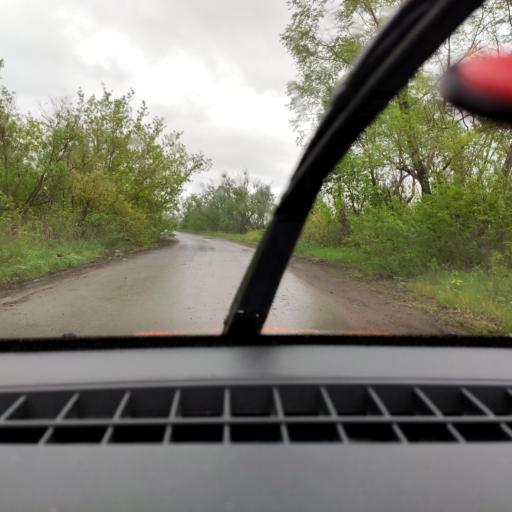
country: RU
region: Bashkortostan
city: Avdon
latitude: 54.5791
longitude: 55.8599
